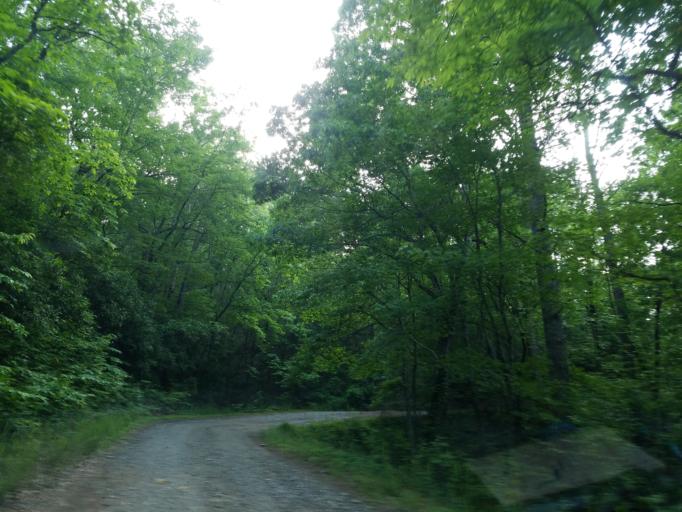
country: US
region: Georgia
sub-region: Dawson County
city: Dawsonville
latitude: 34.5718
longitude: -84.1383
